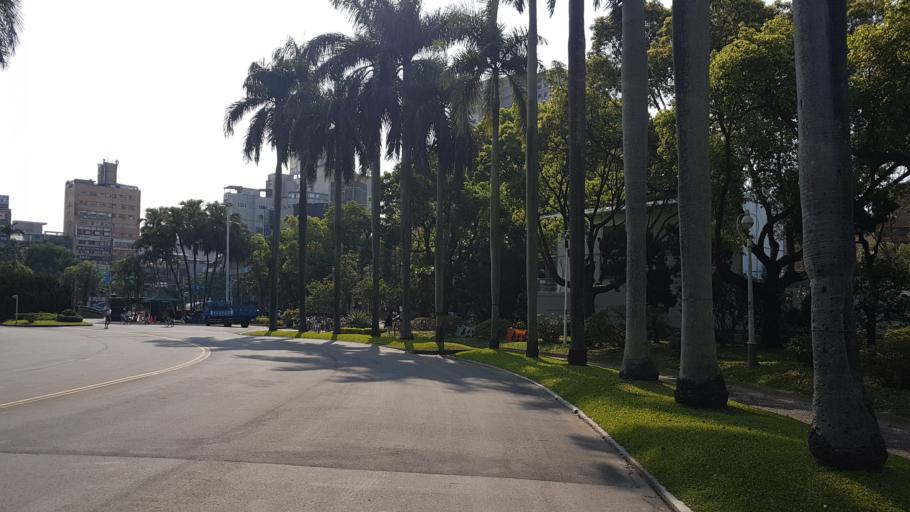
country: TW
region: Taipei
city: Taipei
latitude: 25.0173
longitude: 121.5345
